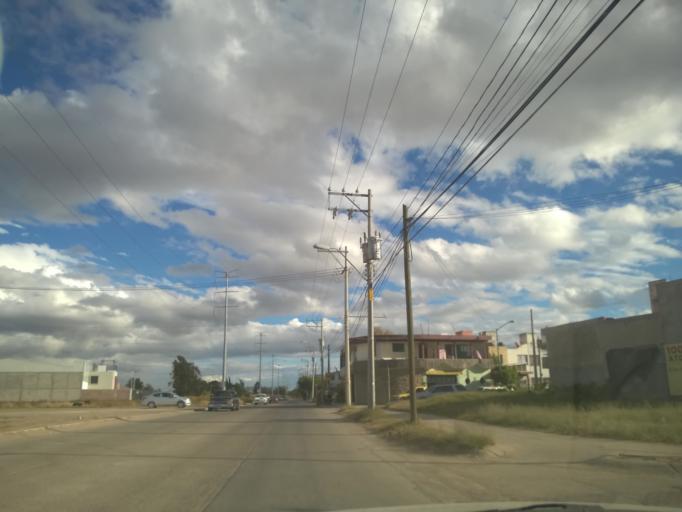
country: MX
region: Guanajuato
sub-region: Leon
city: Fraccionamiento Paraiso Real
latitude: 21.0727
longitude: -101.6127
